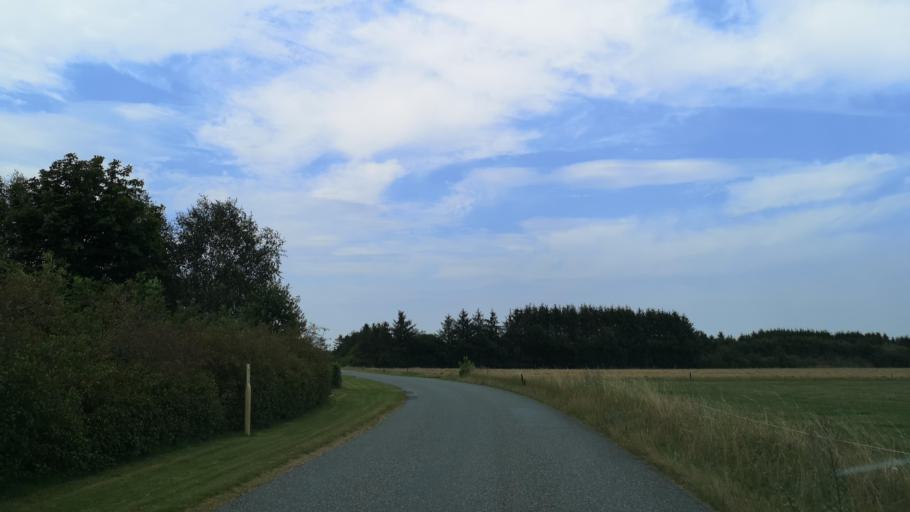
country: DK
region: Central Jutland
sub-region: Ringkobing-Skjern Kommune
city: Videbaek
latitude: 56.0473
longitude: 8.6900
